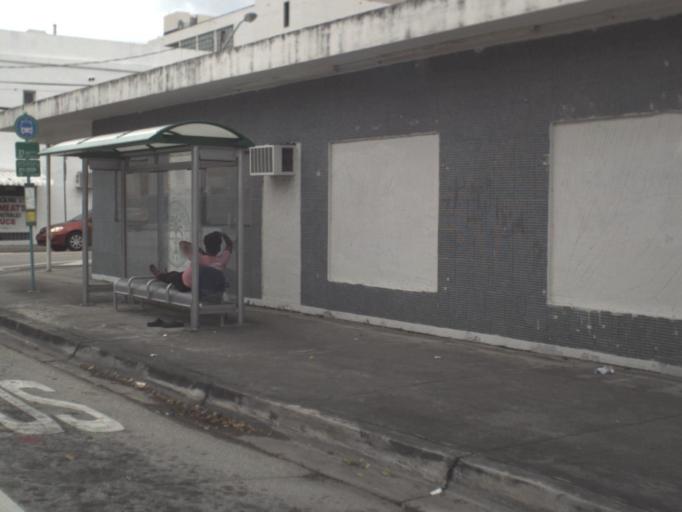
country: US
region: Florida
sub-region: Miami-Dade County
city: Miami
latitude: 25.7787
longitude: -80.2015
